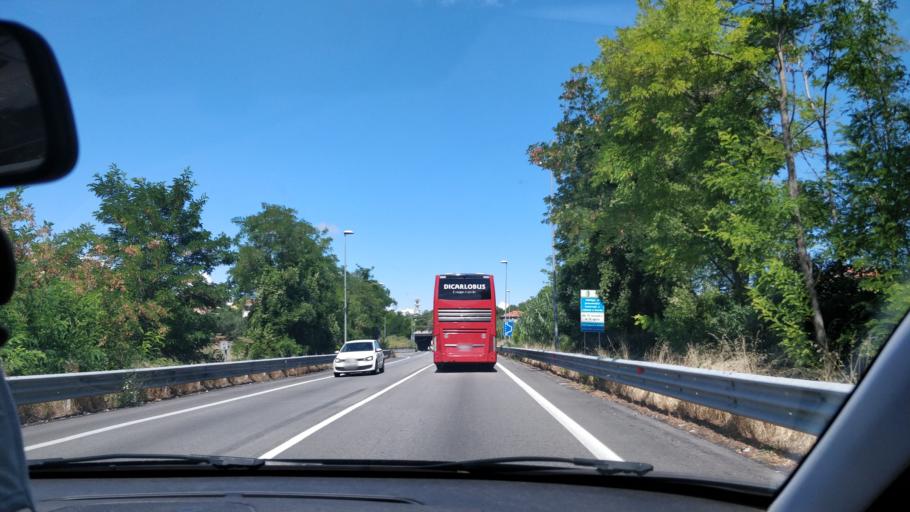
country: IT
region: Abruzzo
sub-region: Provincia di Chieti
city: Francavilla al Mare
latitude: 42.4074
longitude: 14.2995
